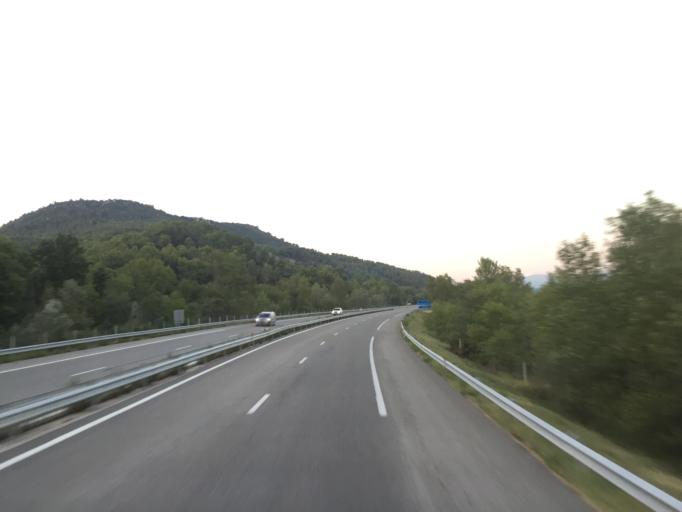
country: FR
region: Provence-Alpes-Cote d'Azur
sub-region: Departement des Alpes-de-Haute-Provence
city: Peyruis
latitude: 43.9812
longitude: 5.9107
